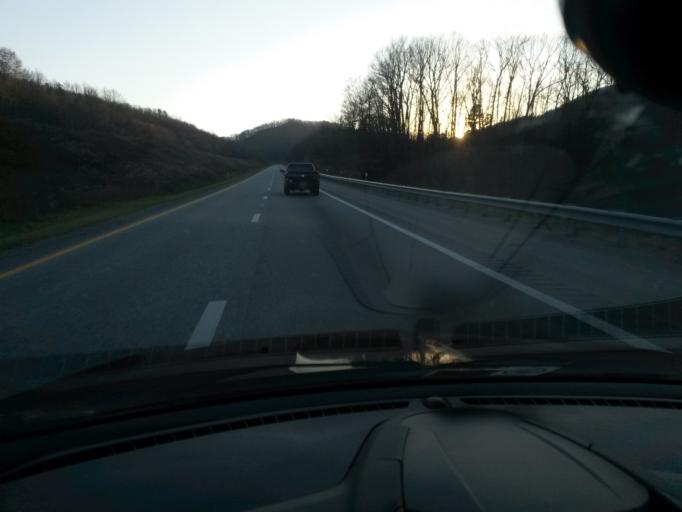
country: US
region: Virginia
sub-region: City of Lexington
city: Lexington
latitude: 37.8795
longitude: -79.6059
